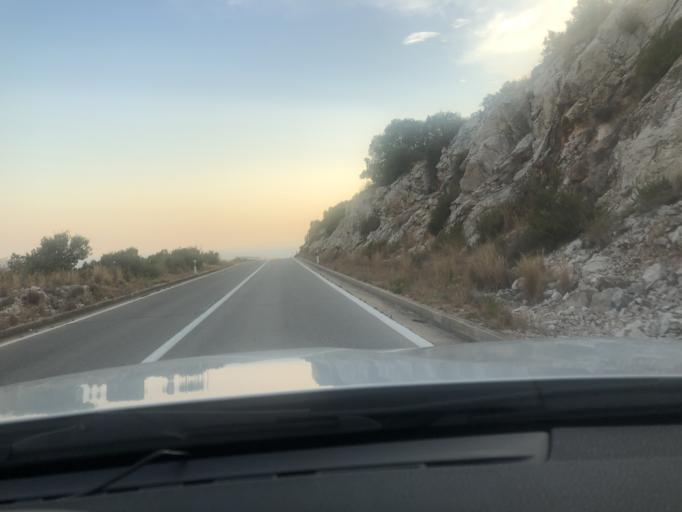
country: HR
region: Splitsko-Dalmatinska
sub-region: Grad Hvar
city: Hvar
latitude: 43.1583
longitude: 16.5061
